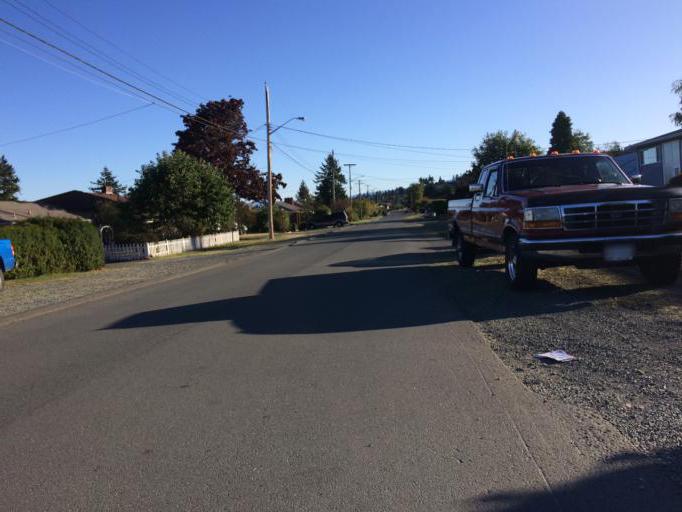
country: CA
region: British Columbia
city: Campbell River
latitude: 50.0128
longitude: -125.2366
